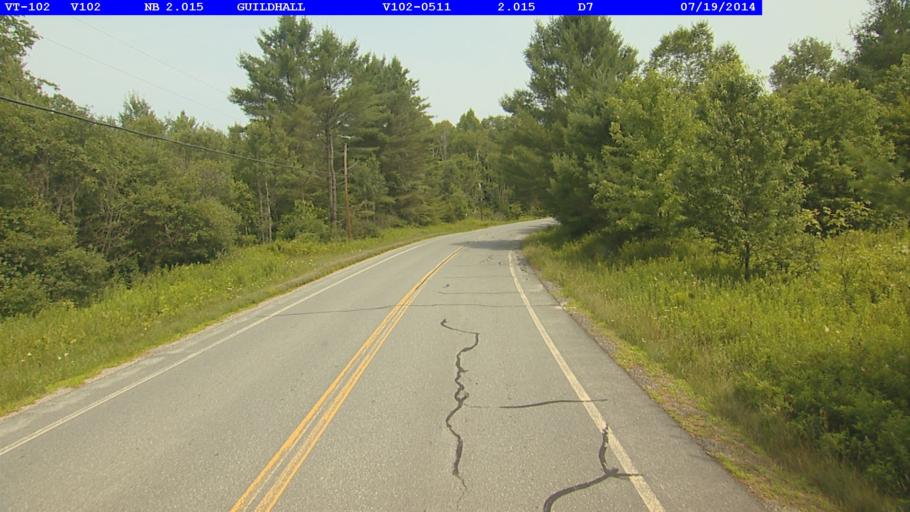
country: US
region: New Hampshire
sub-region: Coos County
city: Lancaster
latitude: 44.5242
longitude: -71.5944
